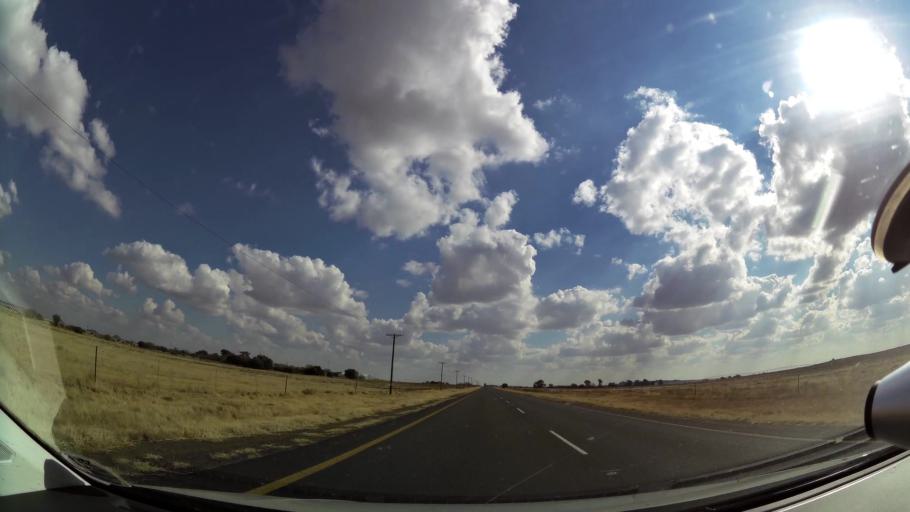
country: ZA
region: Orange Free State
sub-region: Xhariep District Municipality
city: Koffiefontein
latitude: -29.1276
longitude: 25.4855
